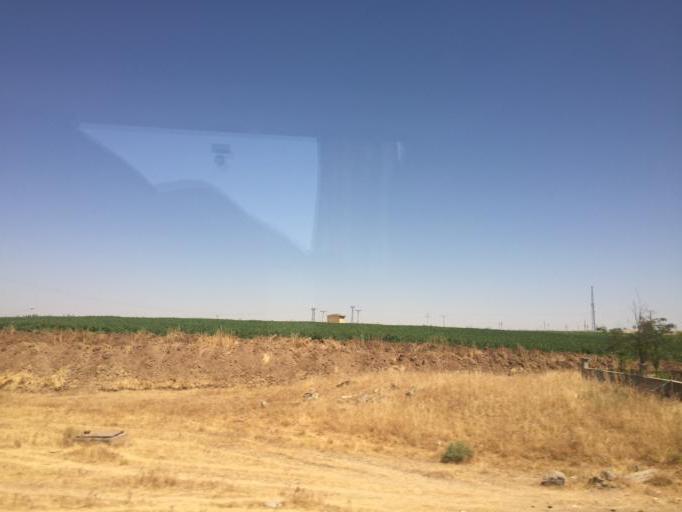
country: TR
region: Diyarbakir
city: Tepe
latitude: 37.8472
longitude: 40.8084
